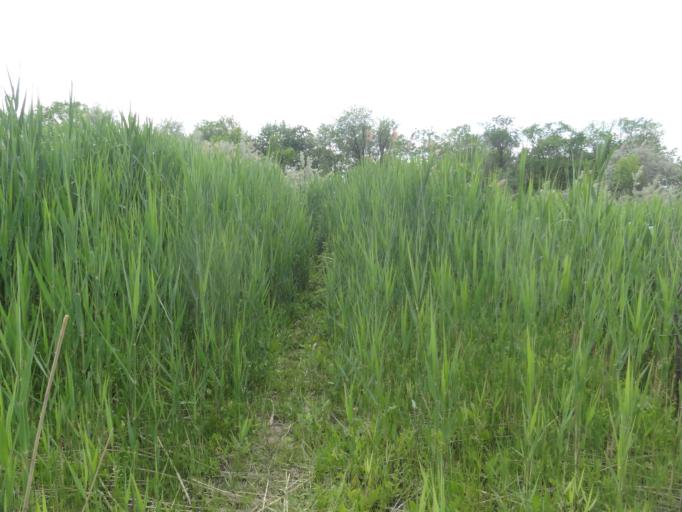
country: RU
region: Saratov
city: Engel's
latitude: 51.4329
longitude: 46.1301
